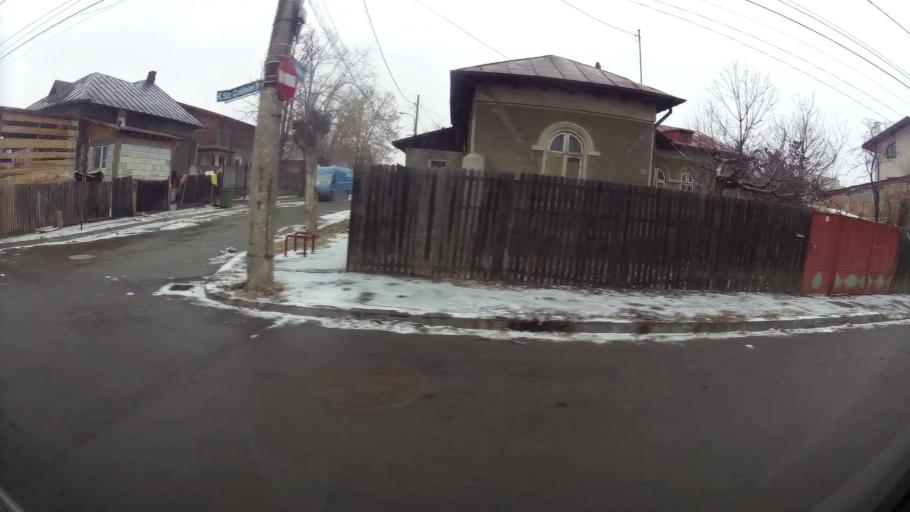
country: RO
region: Prahova
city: Ploiesti
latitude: 44.9519
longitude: 26.0414
